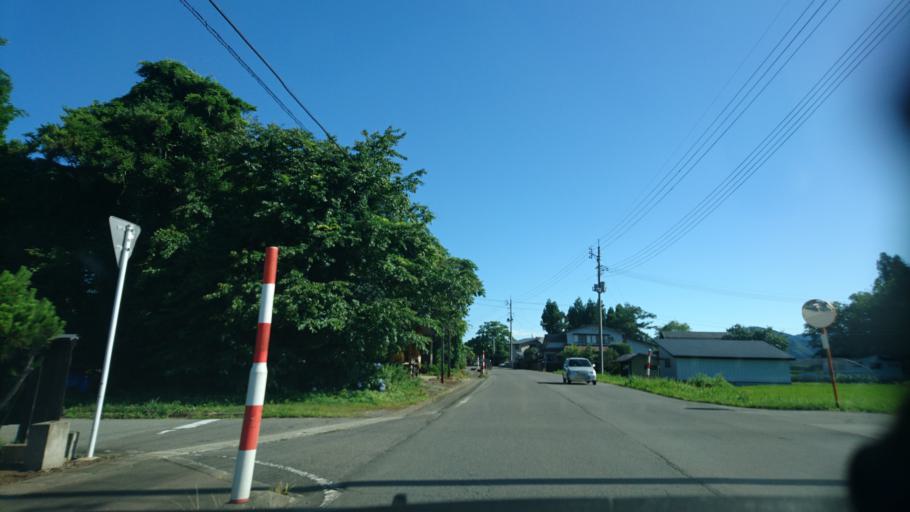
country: JP
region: Akita
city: Kakunodatemachi
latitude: 39.6193
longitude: 140.5719
